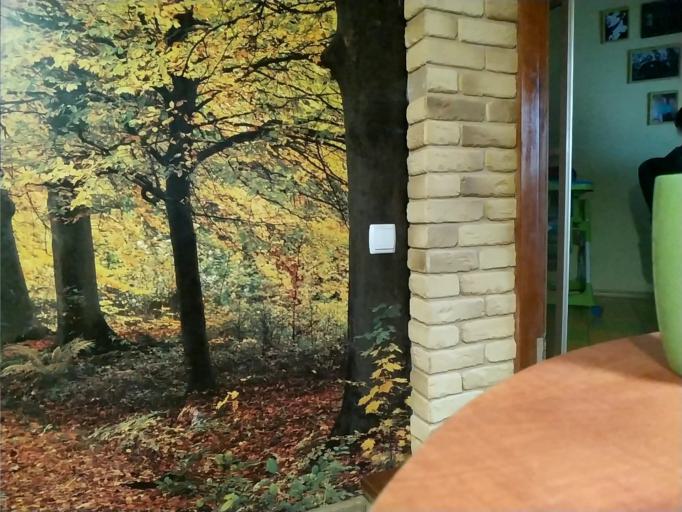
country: RU
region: Tverskaya
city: Staraya Toropa
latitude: 56.3440
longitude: 31.8397
